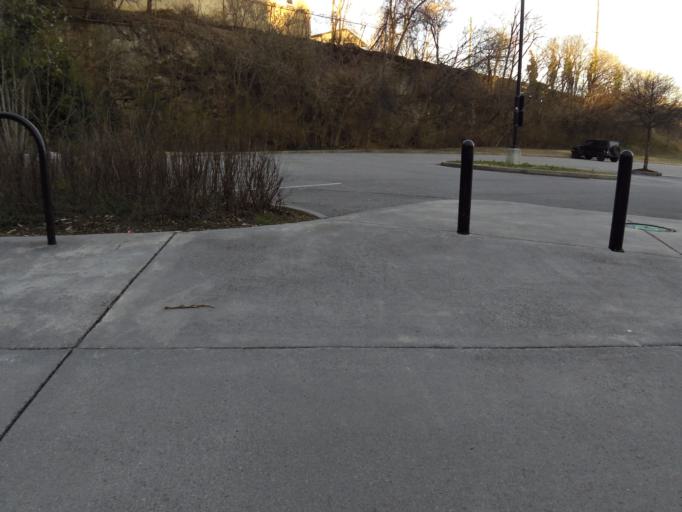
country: US
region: Tennessee
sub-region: Knox County
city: Knoxville
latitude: 35.9569
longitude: -83.9224
